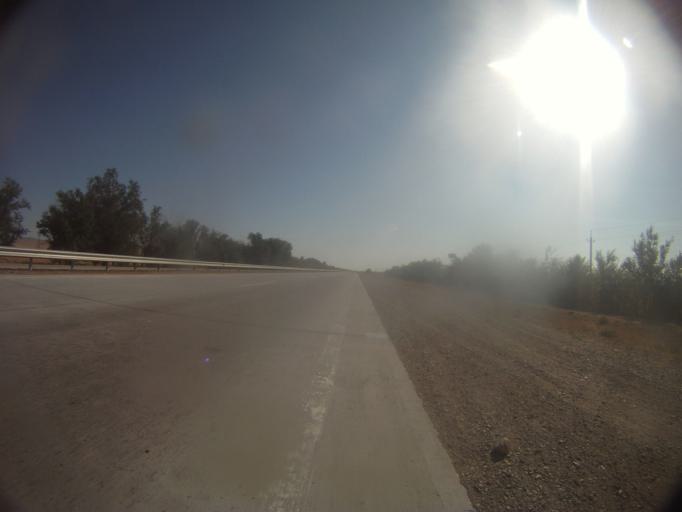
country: KZ
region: Ongtustik Qazaqstan
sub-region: Tulkibas Audany
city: Zhabagly
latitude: 42.7029
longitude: 70.8360
